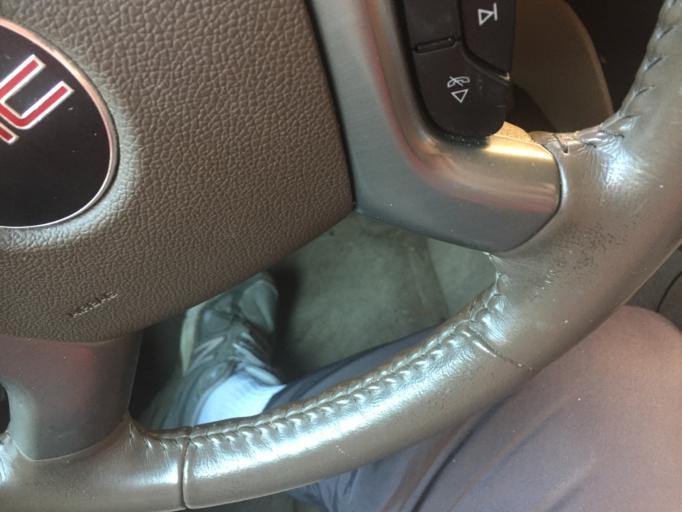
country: US
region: Louisiana
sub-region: Orleans Parish
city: New Orleans
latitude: 29.9394
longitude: -90.0656
